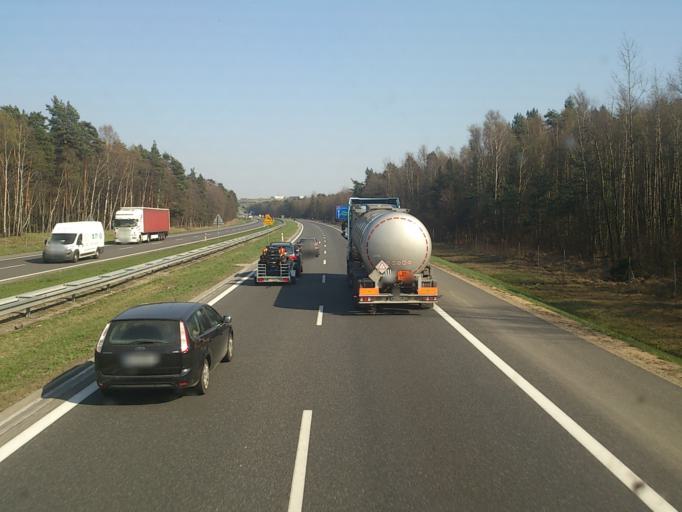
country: PL
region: Lesser Poland Voivodeship
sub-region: Powiat chrzanowski
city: Regulice
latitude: 50.1072
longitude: 19.5184
